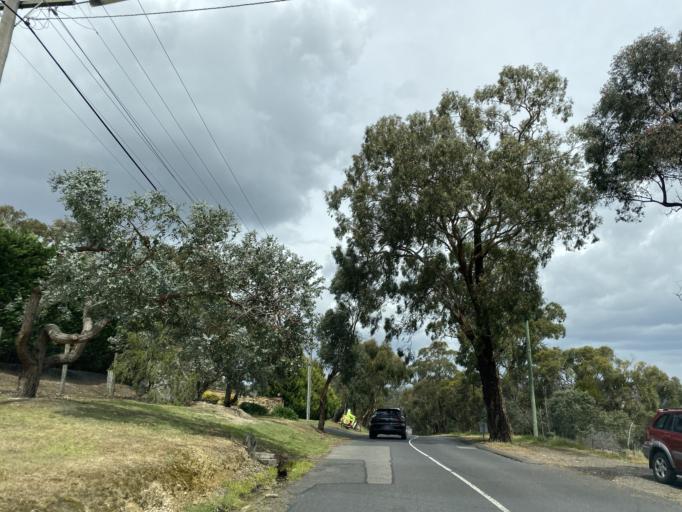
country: AU
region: Victoria
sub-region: Banyule
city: Lower Plenty
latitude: -37.7340
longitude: 145.1194
